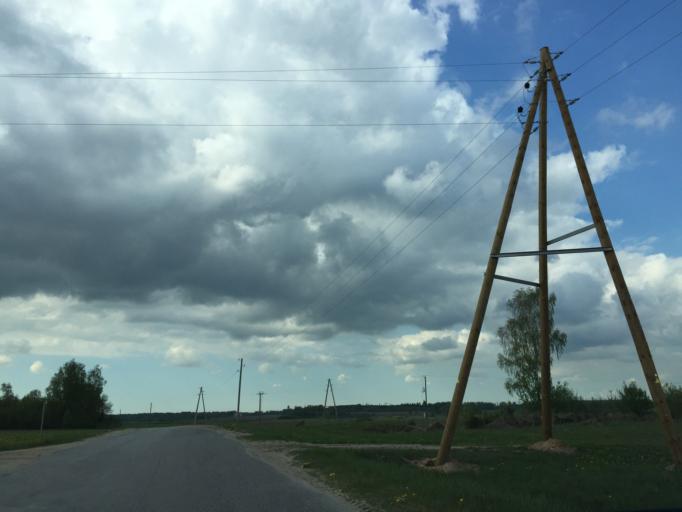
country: LV
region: Krimulda
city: Ragana
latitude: 57.2927
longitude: 24.7857
